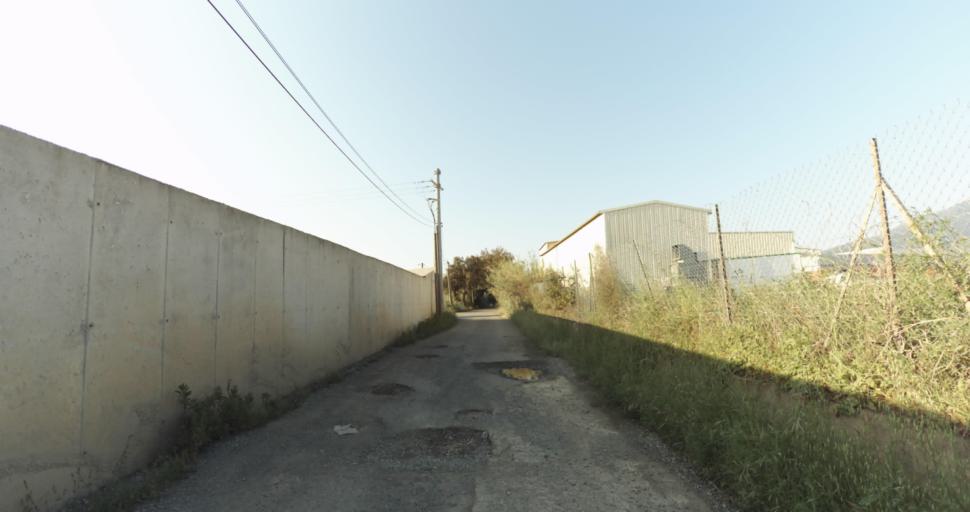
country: FR
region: Corsica
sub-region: Departement de la Haute-Corse
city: Biguglia
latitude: 42.5992
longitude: 9.4460
